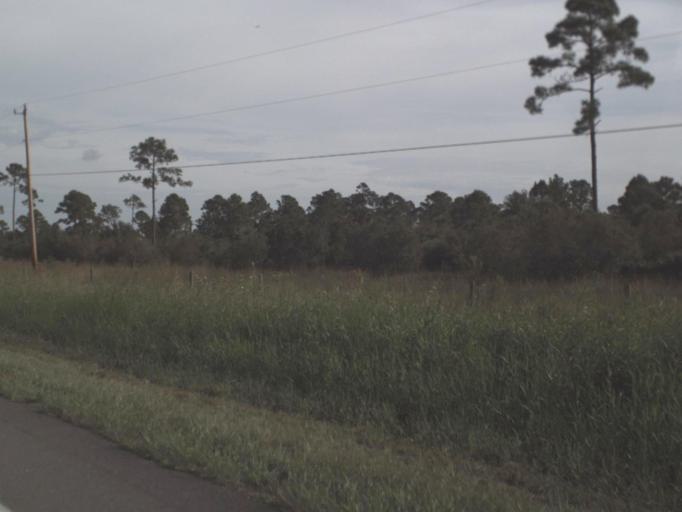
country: US
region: Florida
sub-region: Lee County
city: Olga
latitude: 26.8661
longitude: -81.7597
